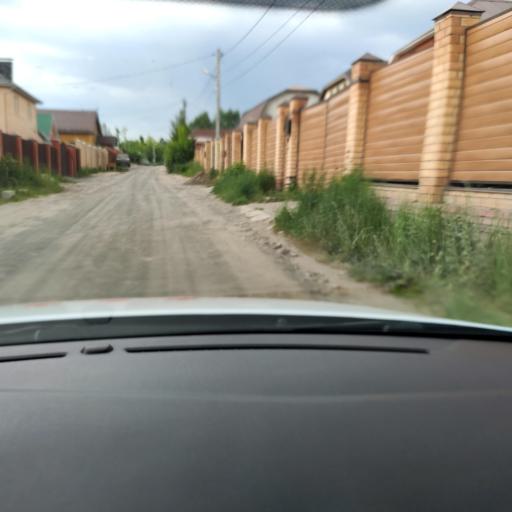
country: RU
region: Tatarstan
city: Stolbishchi
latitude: 55.7500
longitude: 49.2838
